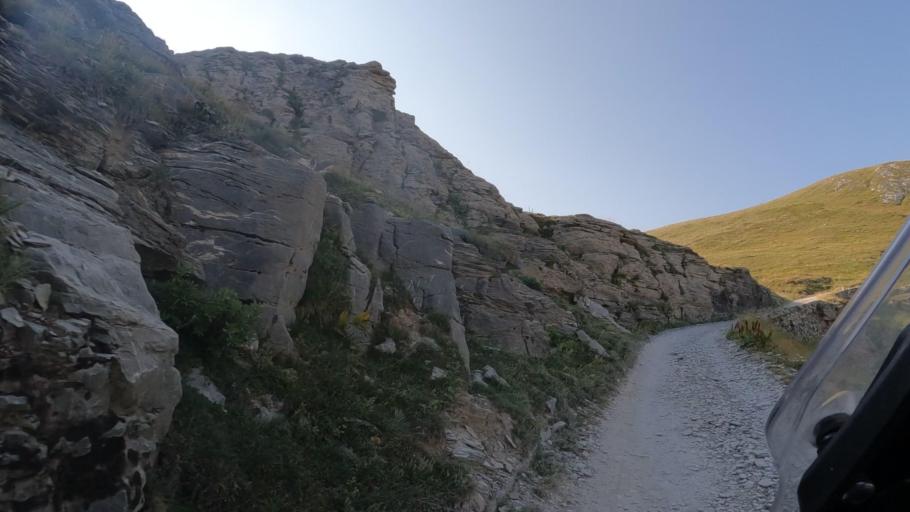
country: IT
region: Piedmont
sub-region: Provincia di Cuneo
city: Limone Piemonte
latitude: 44.1709
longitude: 7.6478
